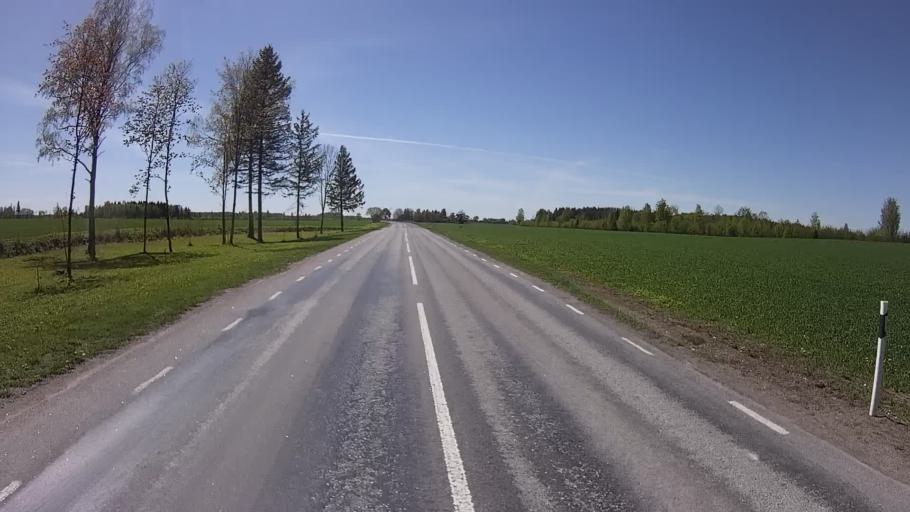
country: EE
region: Harju
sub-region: Raasiku vald
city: Raasiku
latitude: 59.1265
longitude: 25.2000
